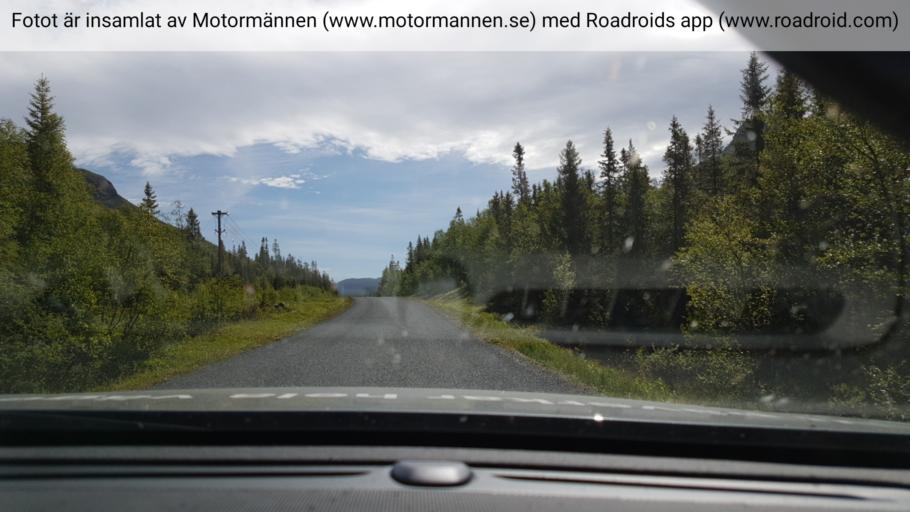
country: SE
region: Vaesterbotten
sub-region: Vilhelmina Kommun
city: Sjoberg
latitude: 65.2477
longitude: 15.4228
